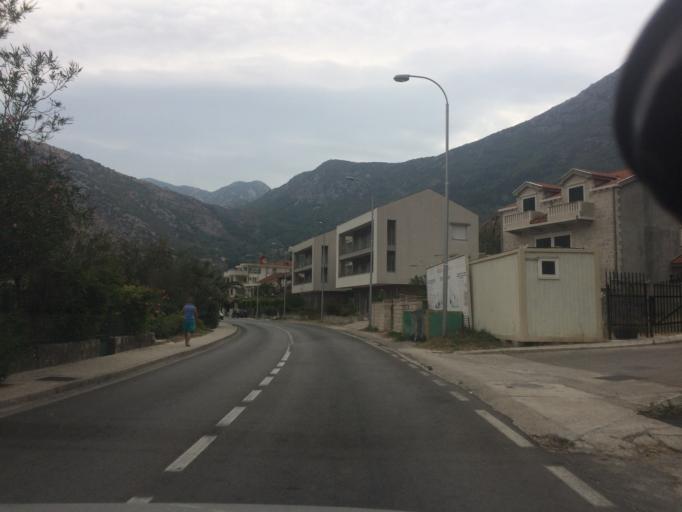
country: ME
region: Kotor
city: Risan
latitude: 42.5092
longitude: 18.6965
